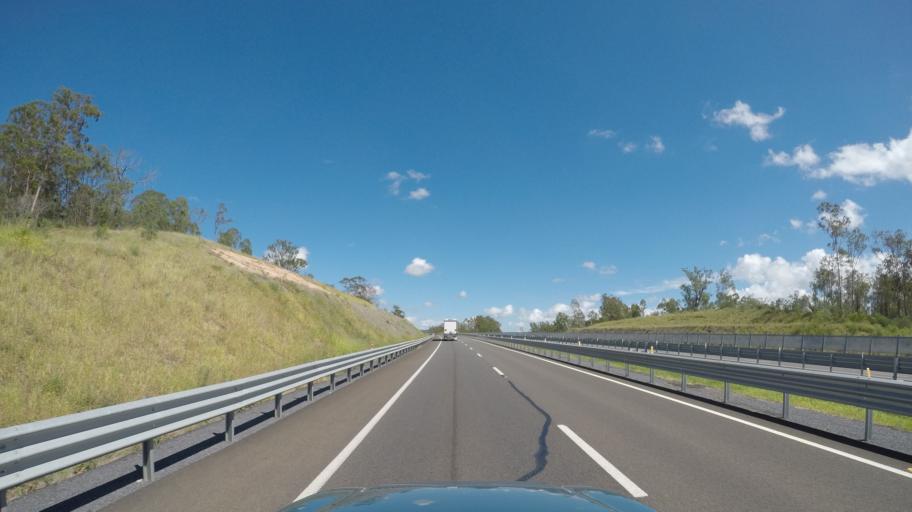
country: AU
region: Queensland
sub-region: Toowoomba
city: East Toowoomba
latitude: -27.5282
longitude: 152.0706
